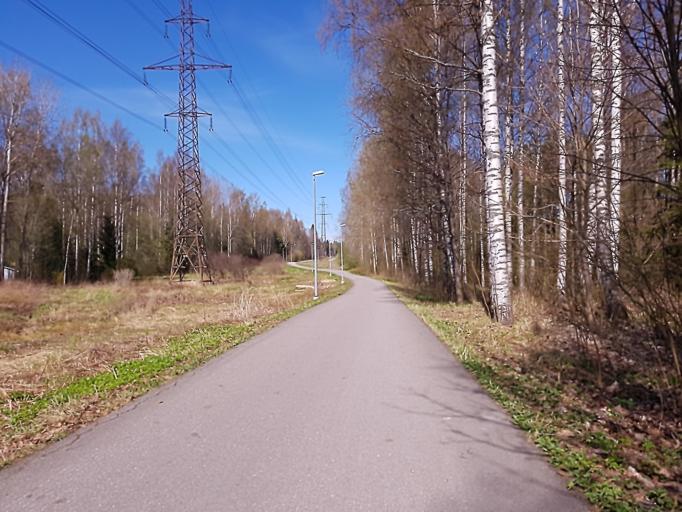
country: FI
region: Uusimaa
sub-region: Helsinki
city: Teekkarikylae
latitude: 60.2514
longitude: 24.8764
